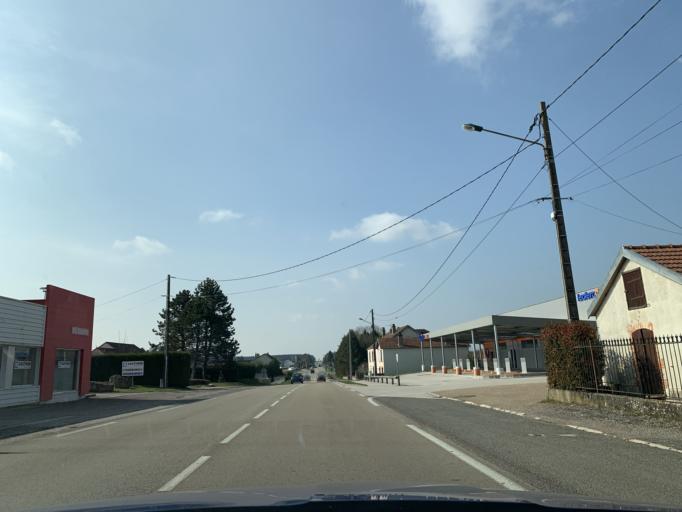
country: FR
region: Champagne-Ardenne
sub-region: Departement de la Haute-Marne
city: Langres
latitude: 47.8385
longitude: 5.3319
